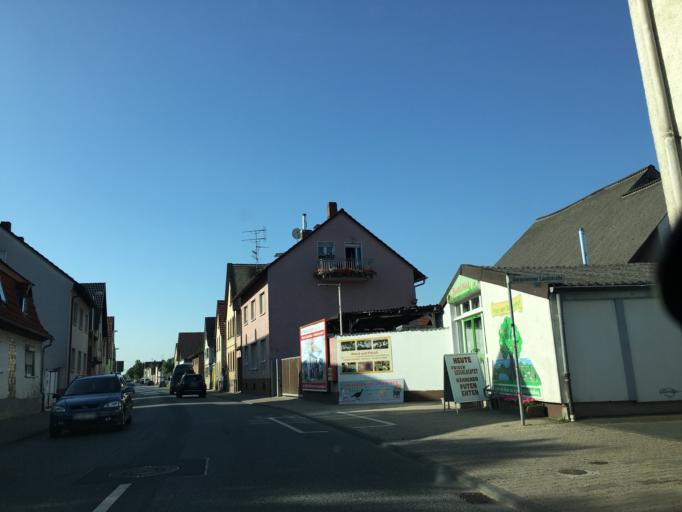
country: DE
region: Hesse
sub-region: Regierungsbezirk Darmstadt
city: Gross-Gerau
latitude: 49.8766
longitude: 8.4819
